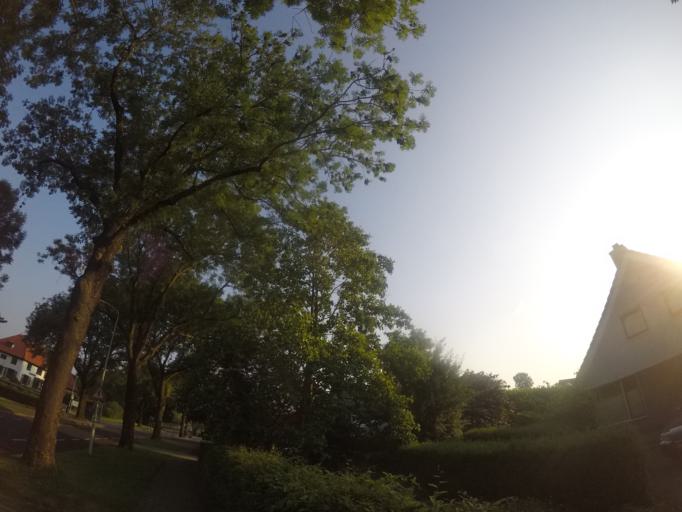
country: NL
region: Gelderland
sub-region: Gemeente Westervoort
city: Westervoort
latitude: 51.9527
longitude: 5.9714
